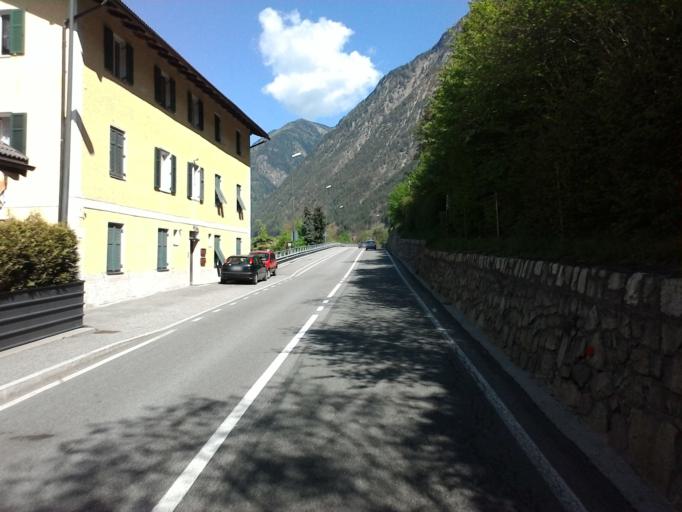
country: IT
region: Trentino-Alto Adige
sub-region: Bolzano
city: Fortezza
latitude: 46.7899
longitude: 11.6119
